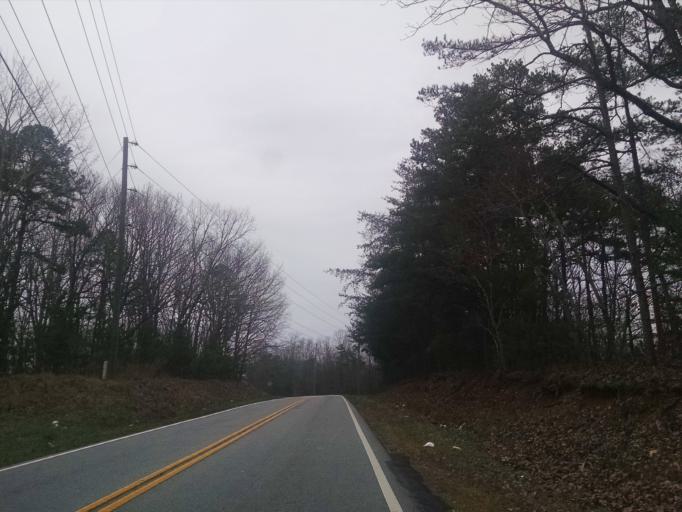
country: US
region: Georgia
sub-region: Hall County
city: Flowery Branch
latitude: 34.1855
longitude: -83.8992
